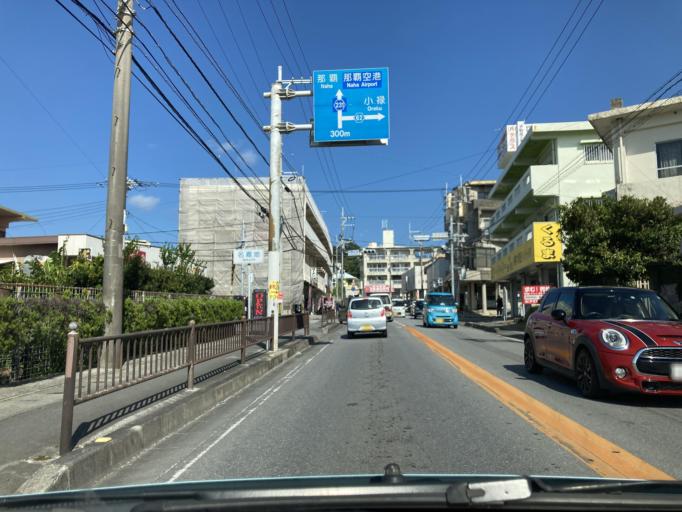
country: JP
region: Okinawa
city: Tomigusuku
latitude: 26.1788
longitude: 127.6649
